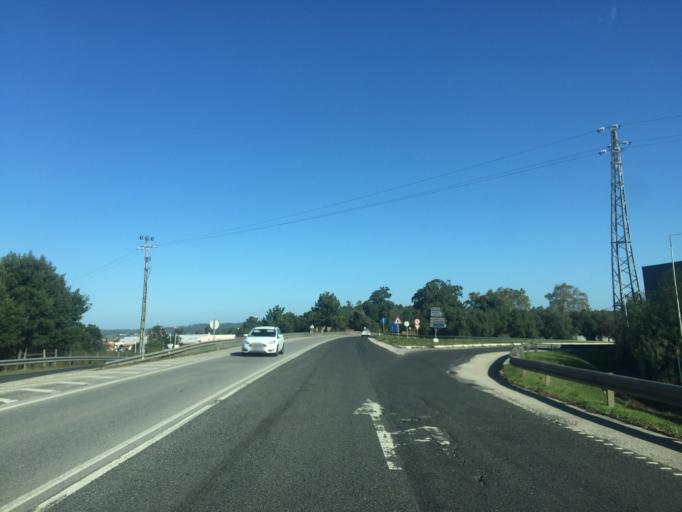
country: PT
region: Leiria
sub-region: Leiria
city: Leiria
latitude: 39.7622
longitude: -8.8163
